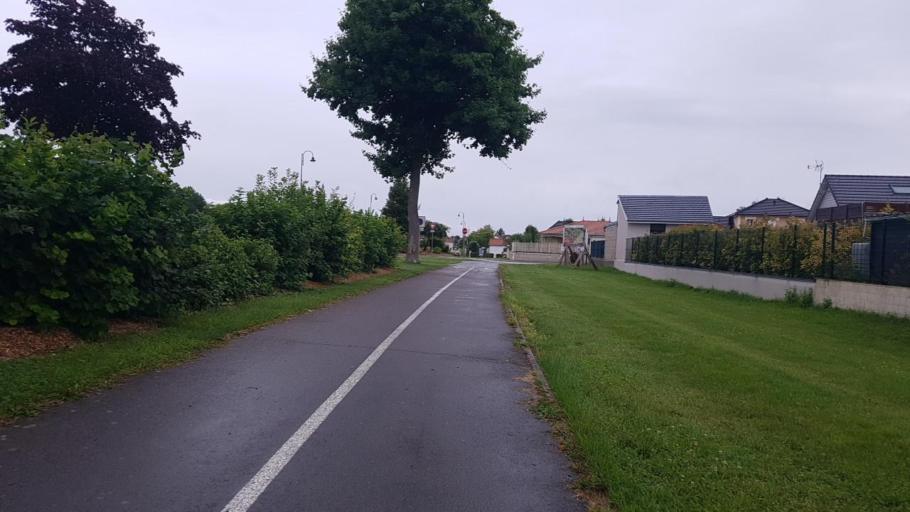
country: FR
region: Champagne-Ardenne
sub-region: Departement de la Marne
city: Sarry
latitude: 48.9139
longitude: 4.4154
